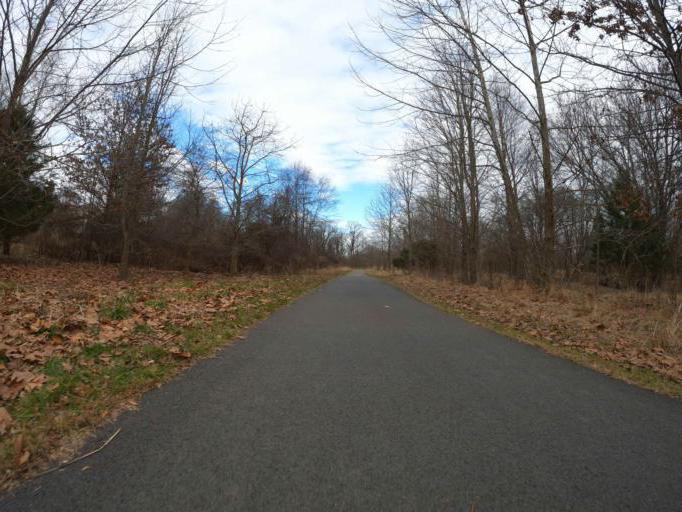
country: US
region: Maryland
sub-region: Frederick County
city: Ballenger Creek
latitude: 39.3718
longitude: -77.4177
